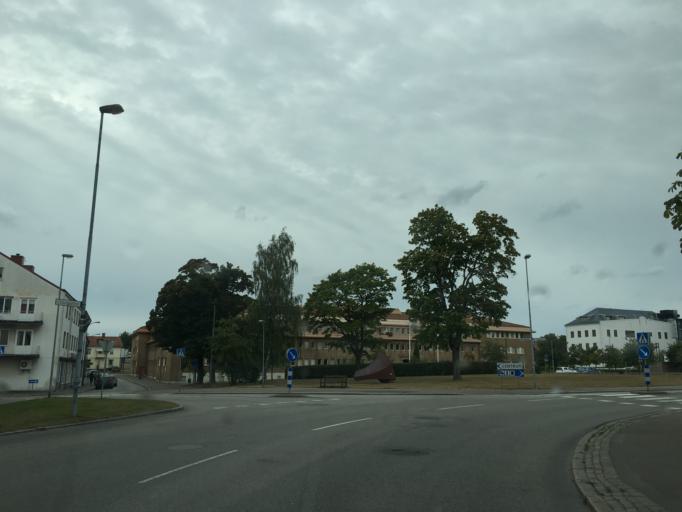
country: SE
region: Kalmar
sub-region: Nybro Kommun
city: Nybro
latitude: 56.7441
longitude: 15.9134
